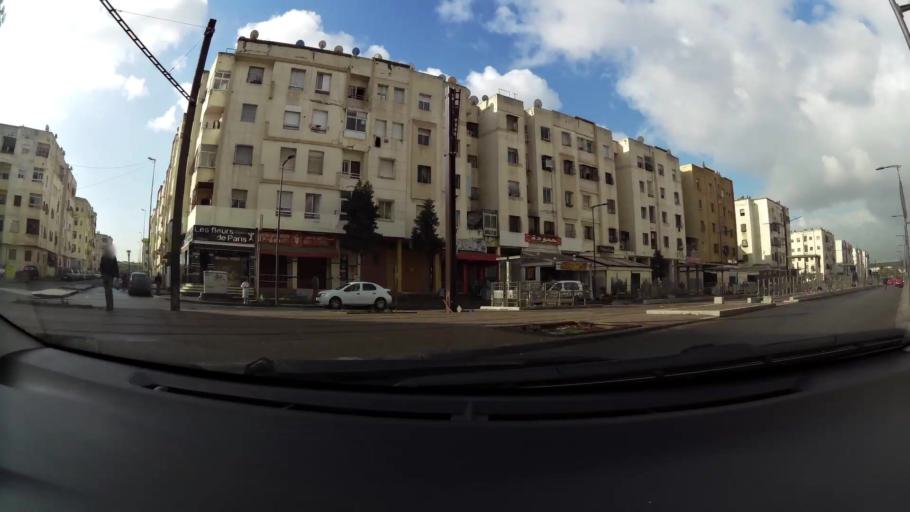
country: MA
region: Grand Casablanca
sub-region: Mediouna
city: Tit Mellil
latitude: 33.5960
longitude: -7.5374
